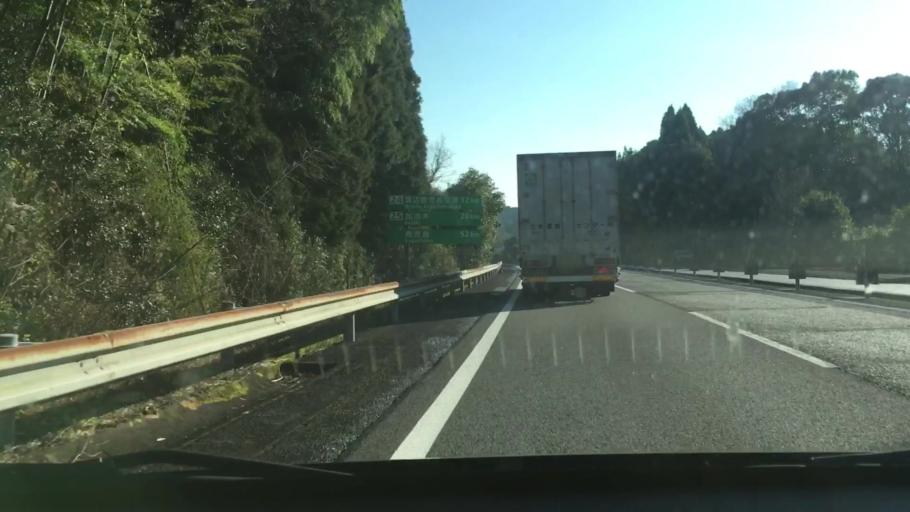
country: JP
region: Kagoshima
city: Kajiki
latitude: 31.8855
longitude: 130.6958
